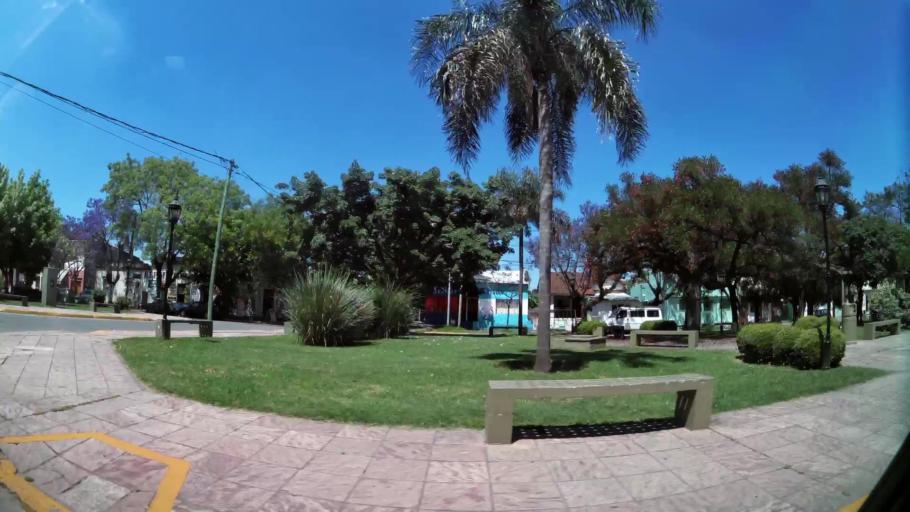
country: AR
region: Buenos Aires
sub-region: Partido de Tigre
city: Tigre
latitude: -34.4323
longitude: -58.5720
